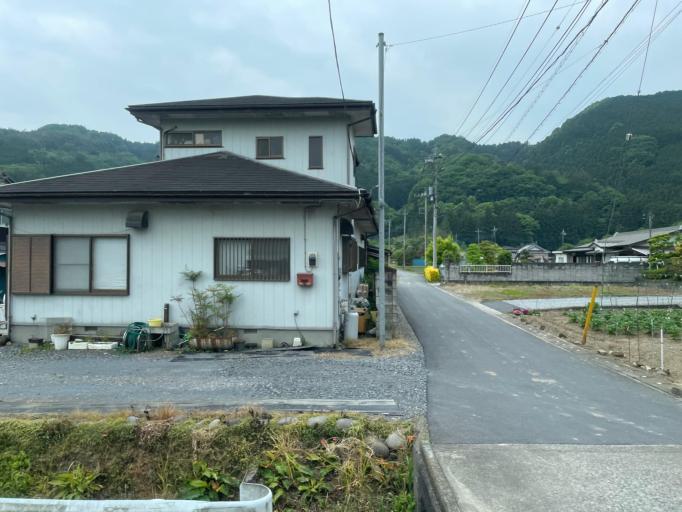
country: JP
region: Tochigi
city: Tochigi
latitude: 36.4385
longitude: 139.6566
